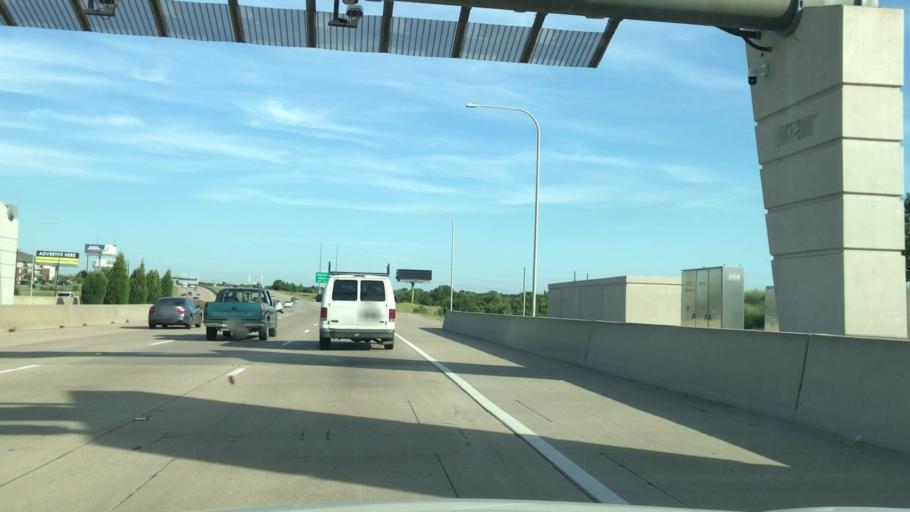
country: US
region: Texas
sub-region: Dallas County
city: Rowlett
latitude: 32.9445
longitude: -96.5584
